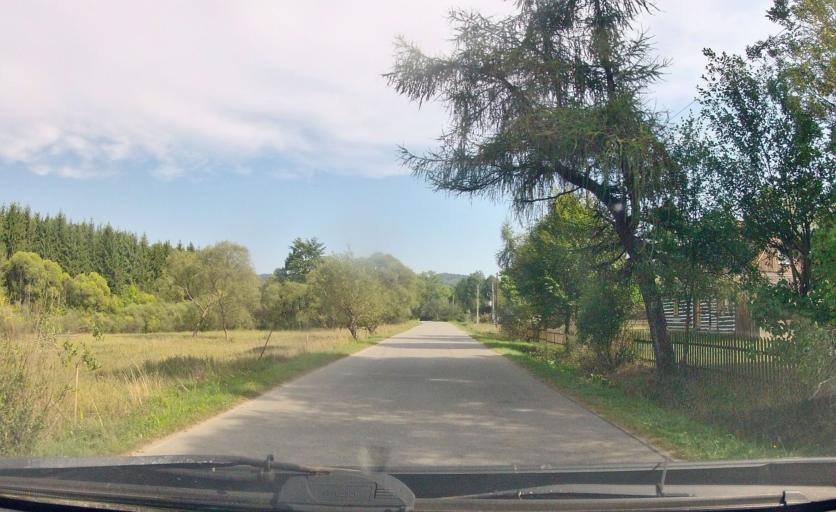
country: PL
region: Subcarpathian Voivodeship
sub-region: Powiat jasielski
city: Krempna
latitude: 49.4967
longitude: 21.5552
